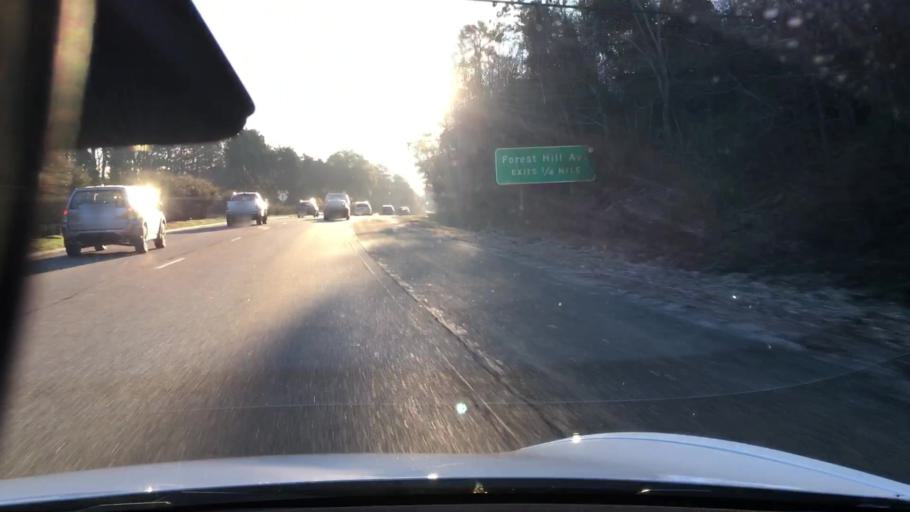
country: US
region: Virginia
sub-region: Chesterfield County
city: Bon Air
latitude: 37.5420
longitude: -77.5359
